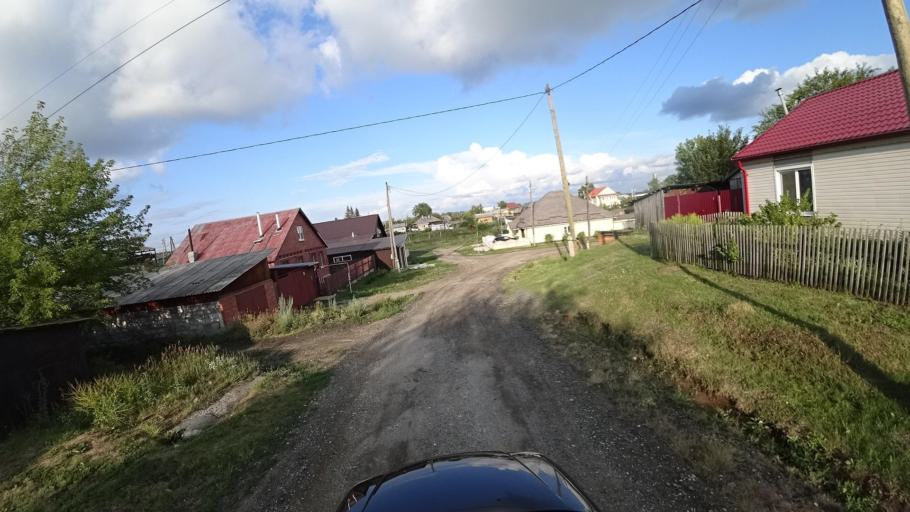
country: RU
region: Sverdlovsk
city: Kamyshlov
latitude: 56.8507
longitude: 62.6702
